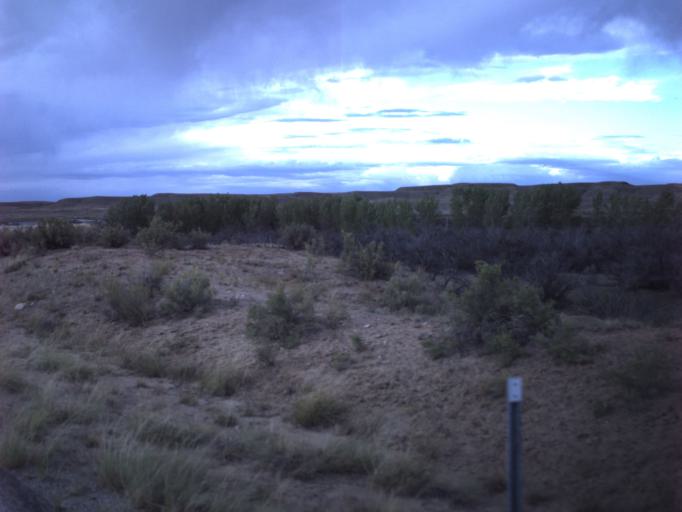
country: US
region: Utah
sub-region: Grand County
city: Moab
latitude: 38.8596
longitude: -109.2939
